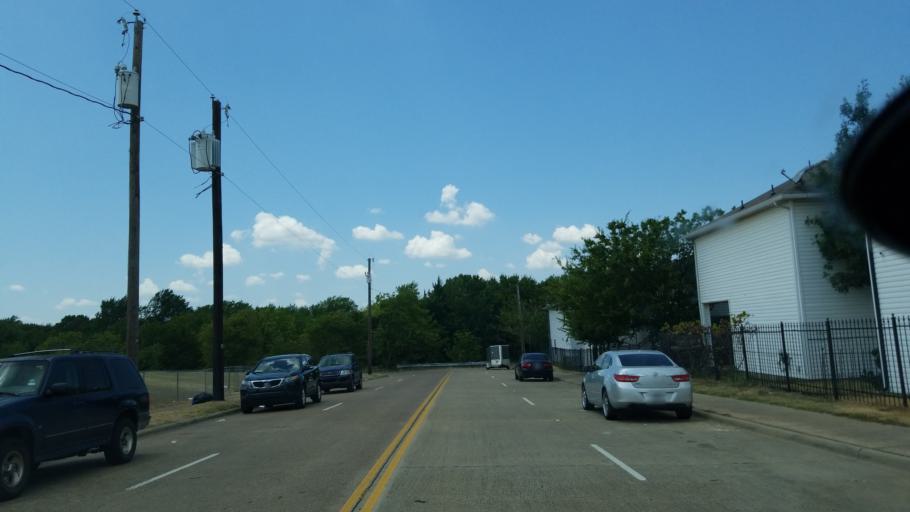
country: US
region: Texas
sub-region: Dallas County
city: Cockrell Hill
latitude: 32.7166
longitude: -96.9021
